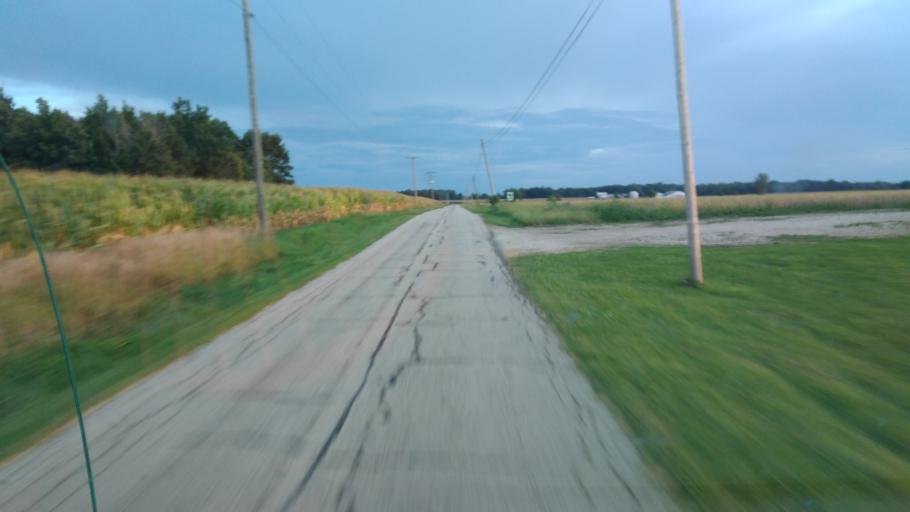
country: US
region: Ohio
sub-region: Crawford County
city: Bucyrus
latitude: 40.7104
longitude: -82.9188
